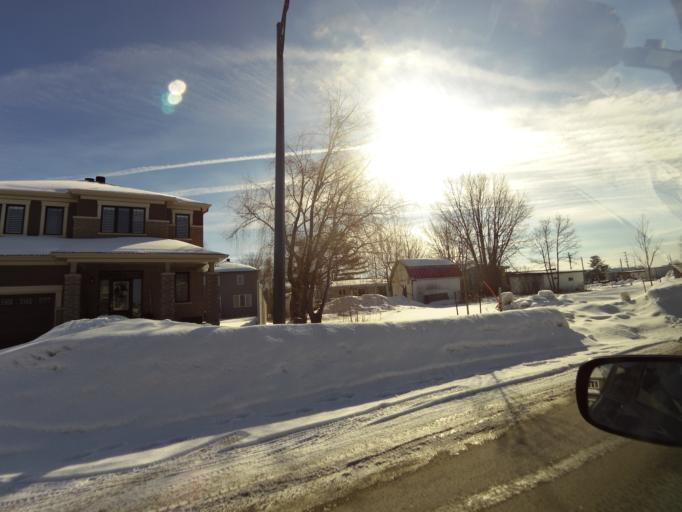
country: CA
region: Ontario
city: Ottawa
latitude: 45.4342
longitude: -75.5085
